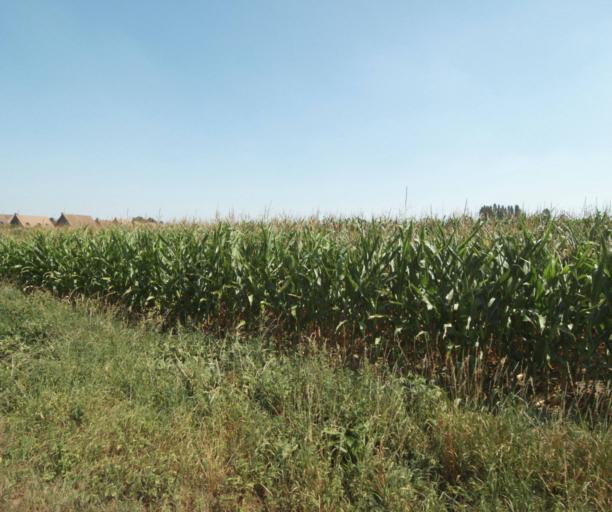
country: FR
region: Nord-Pas-de-Calais
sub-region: Departement du Nord
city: Bousbecque
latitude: 50.7666
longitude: 3.0690
